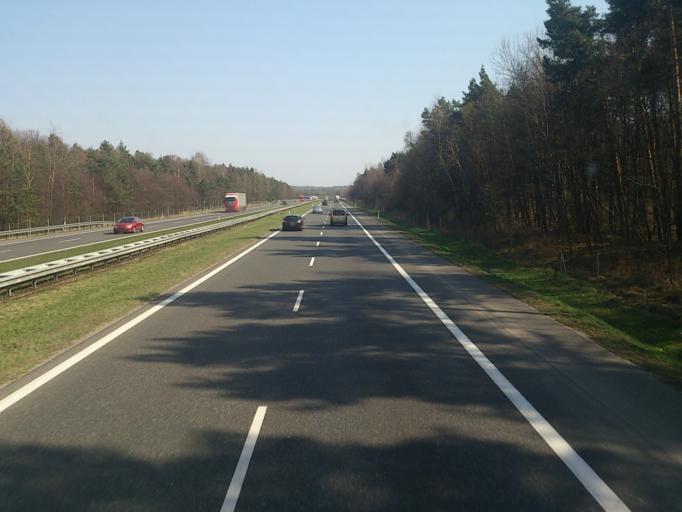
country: PL
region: Lesser Poland Voivodeship
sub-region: Powiat chrzanowski
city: Bolecin
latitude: 50.1184
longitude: 19.4979
